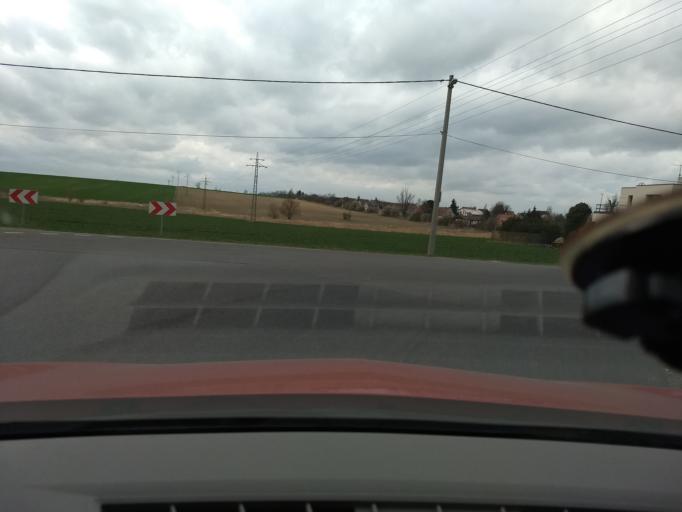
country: CZ
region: Central Bohemia
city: Unhost'
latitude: 50.0860
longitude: 14.1411
